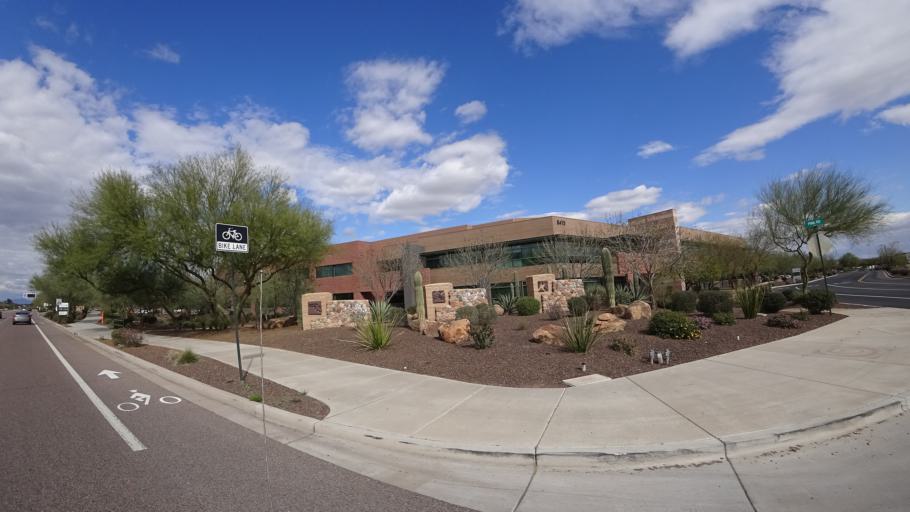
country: US
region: Arizona
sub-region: Maricopa County
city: Scottsdale
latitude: 33.5566
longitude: -111.8913
